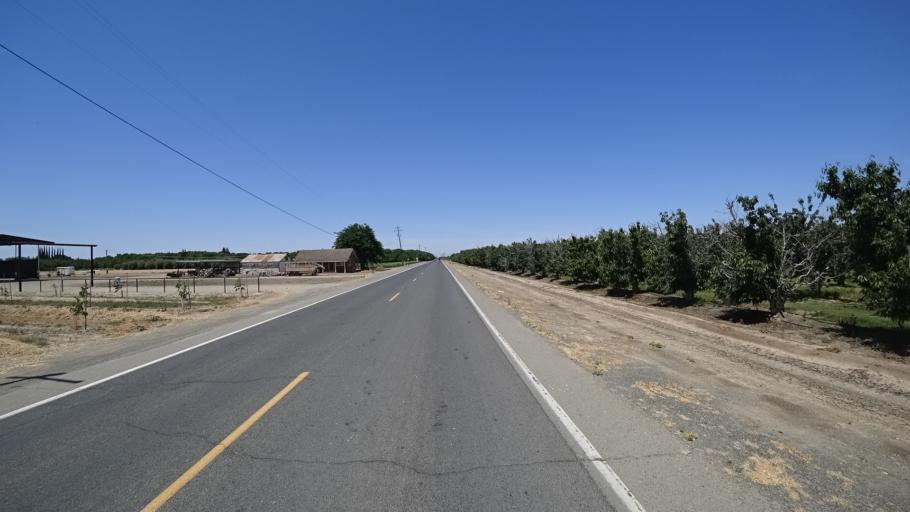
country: US
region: California
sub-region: Kings County
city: Lemoore
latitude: 36.3426
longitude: -119.7595
